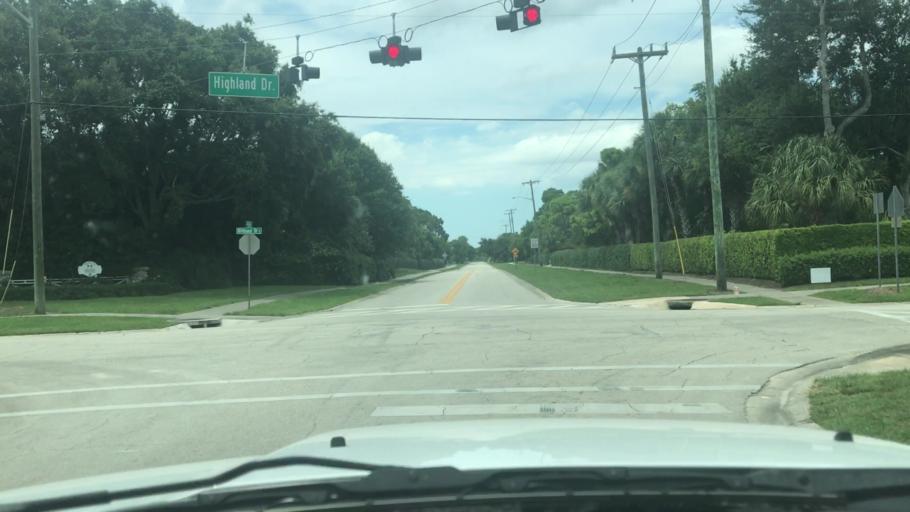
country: US
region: Florida
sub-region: Indian River County
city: Florida Ridge
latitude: 27.5629
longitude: -80.3817
